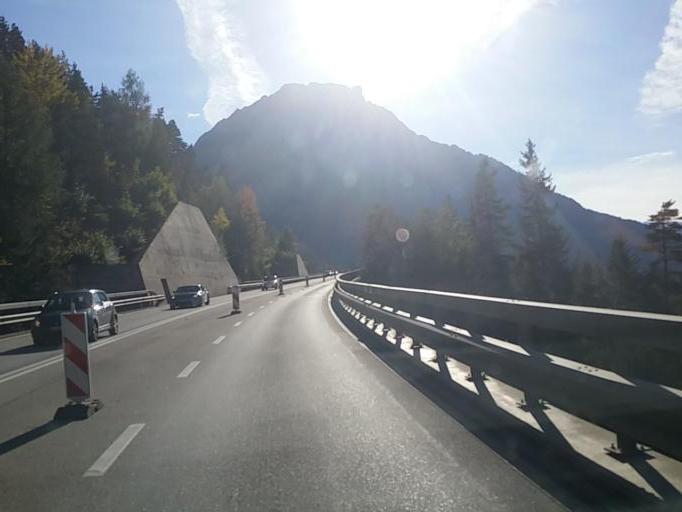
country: CH
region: Valais
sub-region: Brig District
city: Naters
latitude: 46.3093
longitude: 8.0293
